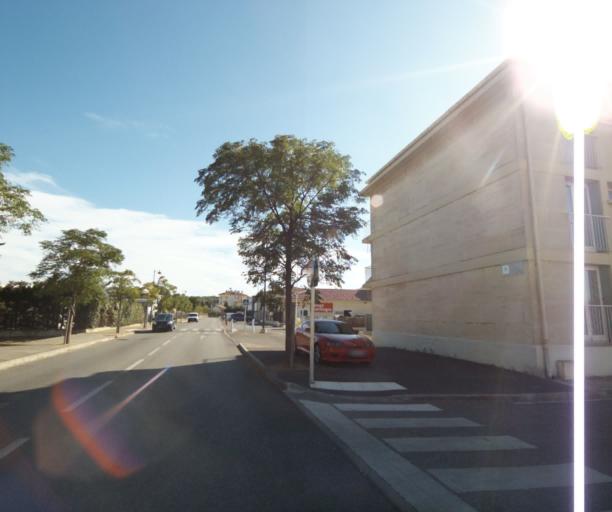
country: FR
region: Provence-Alpes-Cote d'Azur
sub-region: Departement des Bouches-du-Rhone
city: Saint-Victoret
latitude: 43.4179
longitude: 5.2453
